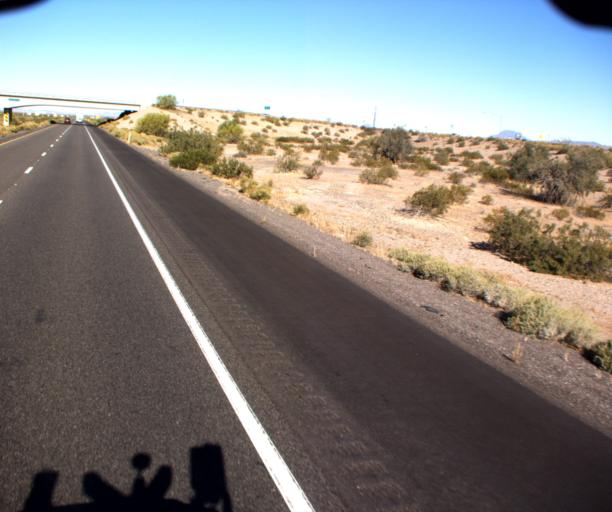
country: US
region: Arizona
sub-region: Maricopa County
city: Gila Bend
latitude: 32.9251
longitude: -112.6694
